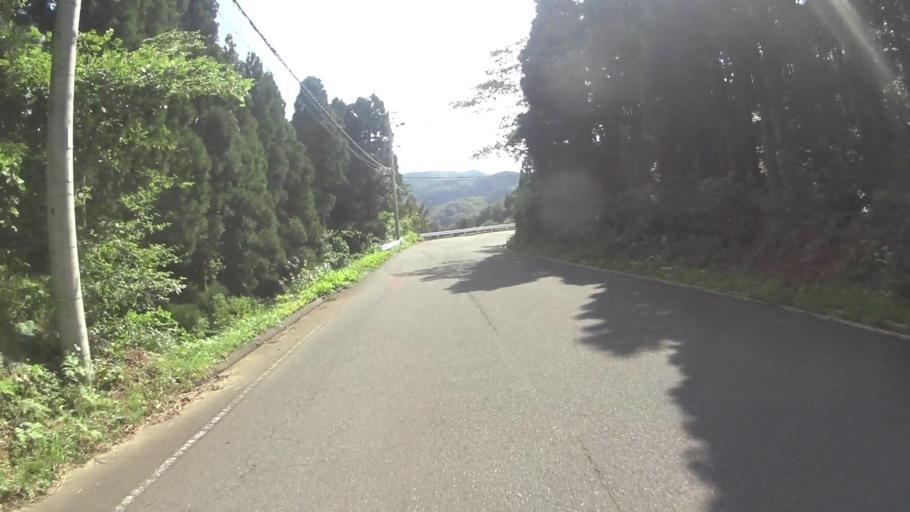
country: JP
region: Kyoto
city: Miyazu
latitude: 35.7153
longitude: 135.1955
